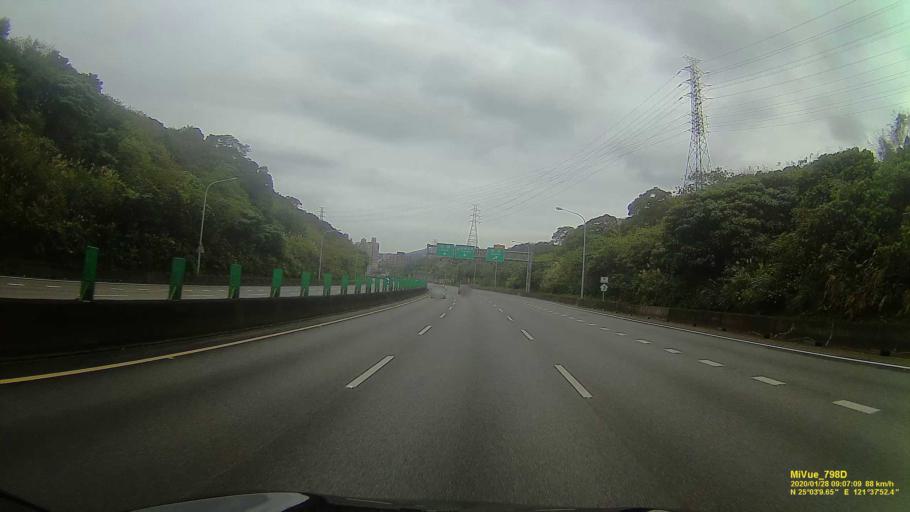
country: TW
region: Taipei
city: Taipei
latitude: 25.0534
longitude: 121.6295
